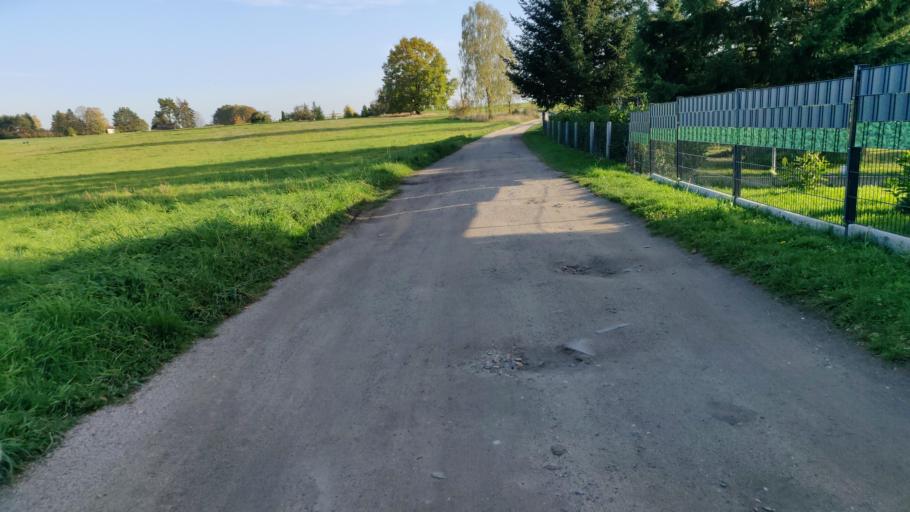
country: DE
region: Brandenburg
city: Ortrand
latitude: 51.3699
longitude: 13.7490
